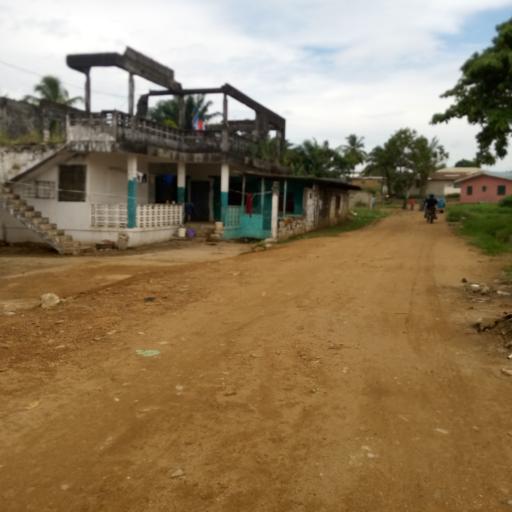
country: LR
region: Montserrado
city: Monrovia
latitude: 6.2961
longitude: -10.6997
